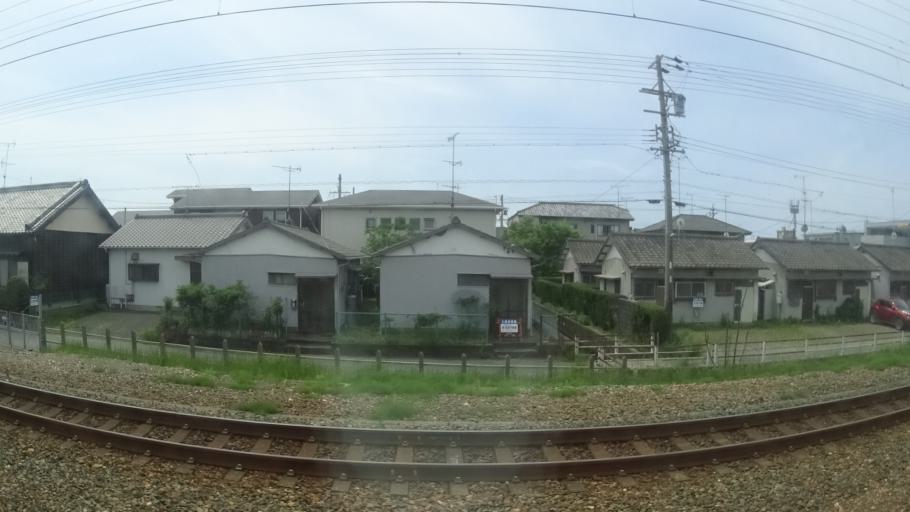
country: JP
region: Shizuoka
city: Kosai-shi
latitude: 34.6857
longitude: 137.6240
